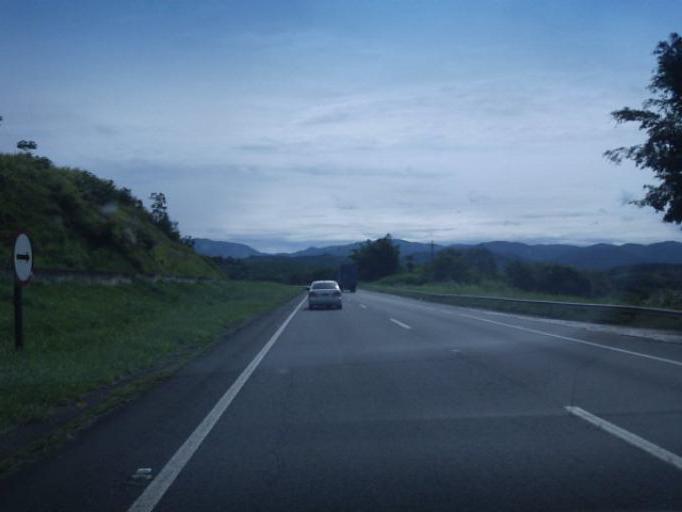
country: BR
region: Sao Paulo
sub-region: Cajati
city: Cajati
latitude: -24.7532
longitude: -48.1585
